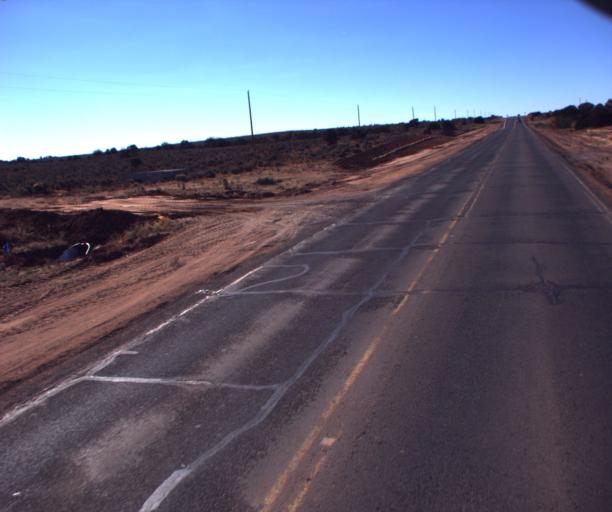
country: US
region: Arizona
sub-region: Apache County
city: Ganado
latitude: 35.7113
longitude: -109.5049
